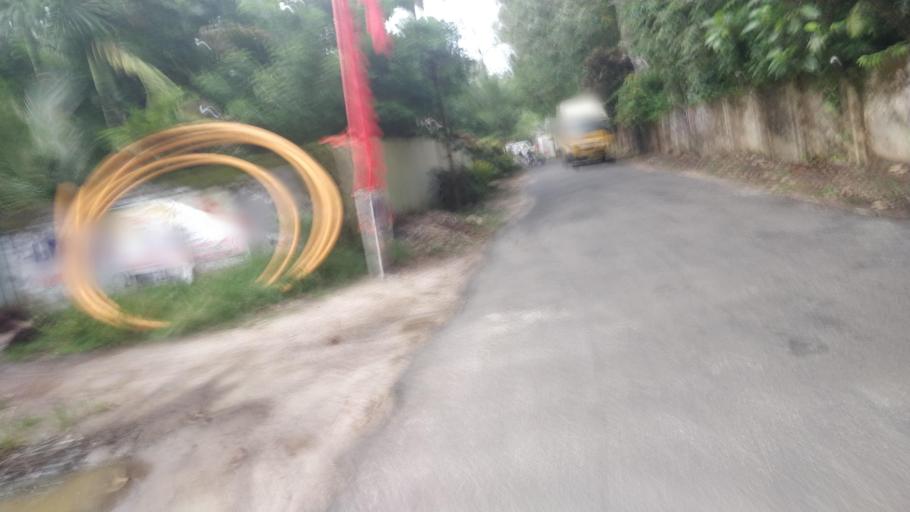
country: IN
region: Kerala
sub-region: Alappuzha
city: Vayalar
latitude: 9.7078
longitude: 76.3489
